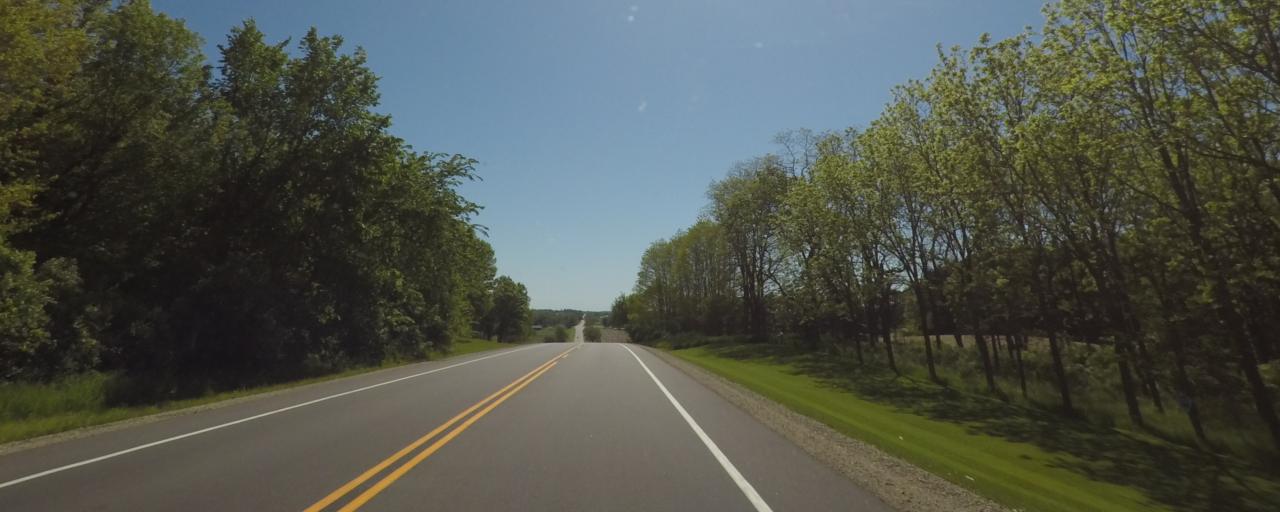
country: US
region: Wisconsin
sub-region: Dane County
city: Fitchburg
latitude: 42.9504
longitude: -89.4527
